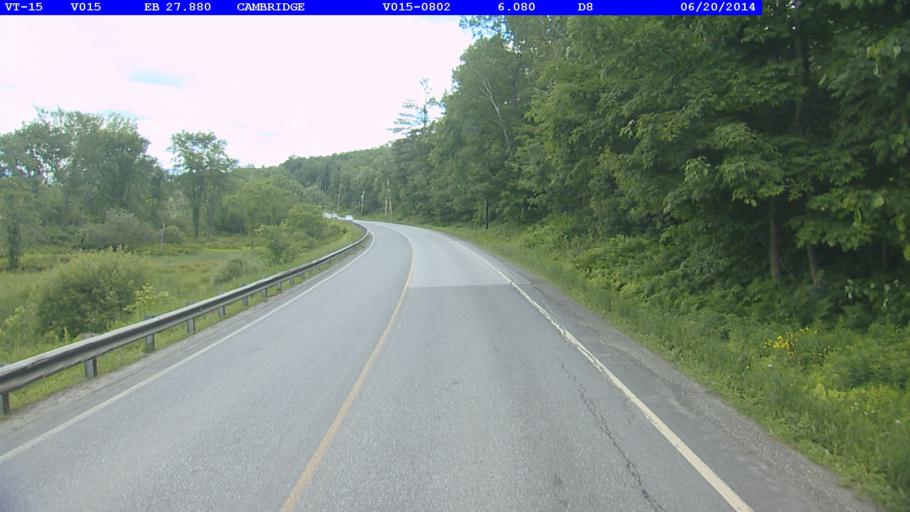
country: US
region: Vermont
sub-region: Lamoille County
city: Johnson
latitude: 44.6497
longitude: -72.8109
